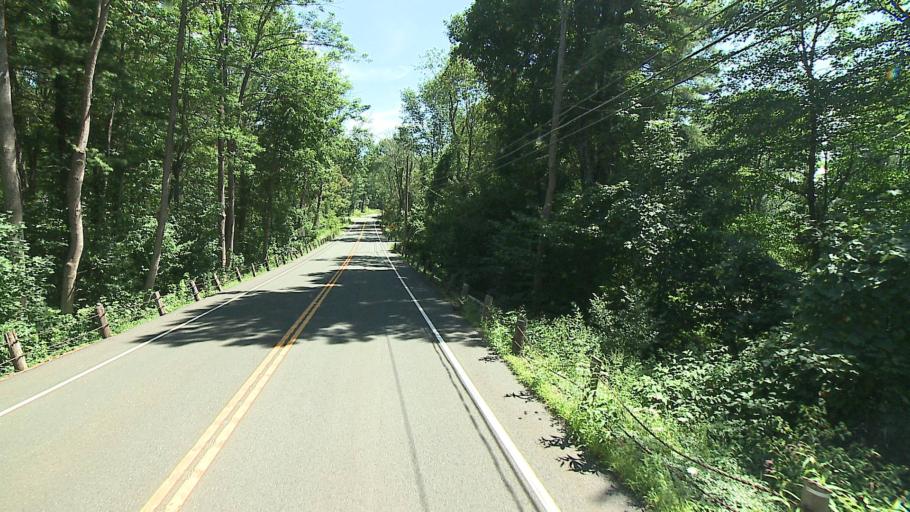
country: US
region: Connecticut
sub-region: Litchfield County
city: New Hartford Center
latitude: 41.9301
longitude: -72.9682
